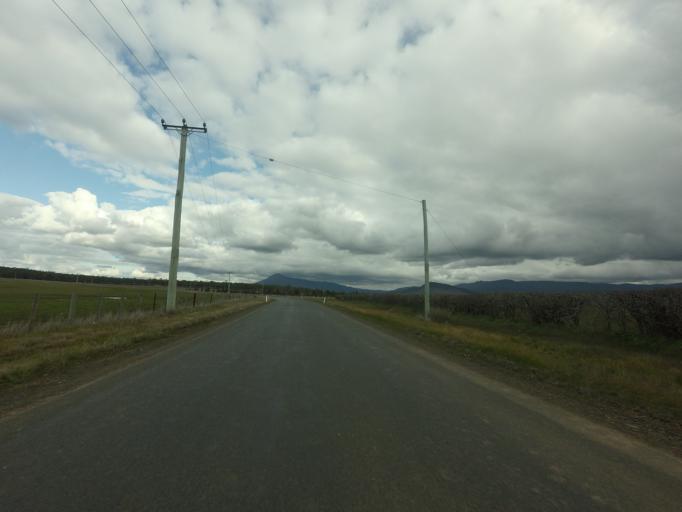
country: AU
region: Tasmania
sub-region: Northern Midlands
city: Longford
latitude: -41.7933
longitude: 147.1136
